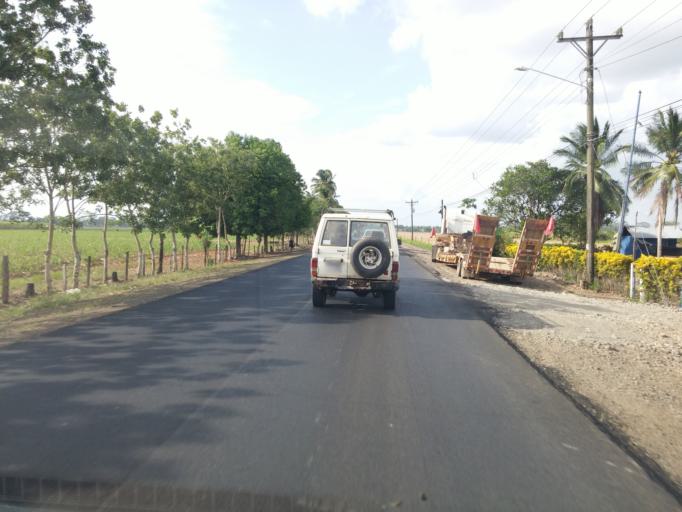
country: CR
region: Alajuela
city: Quesada
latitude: 10.4474
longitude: -84.4652
